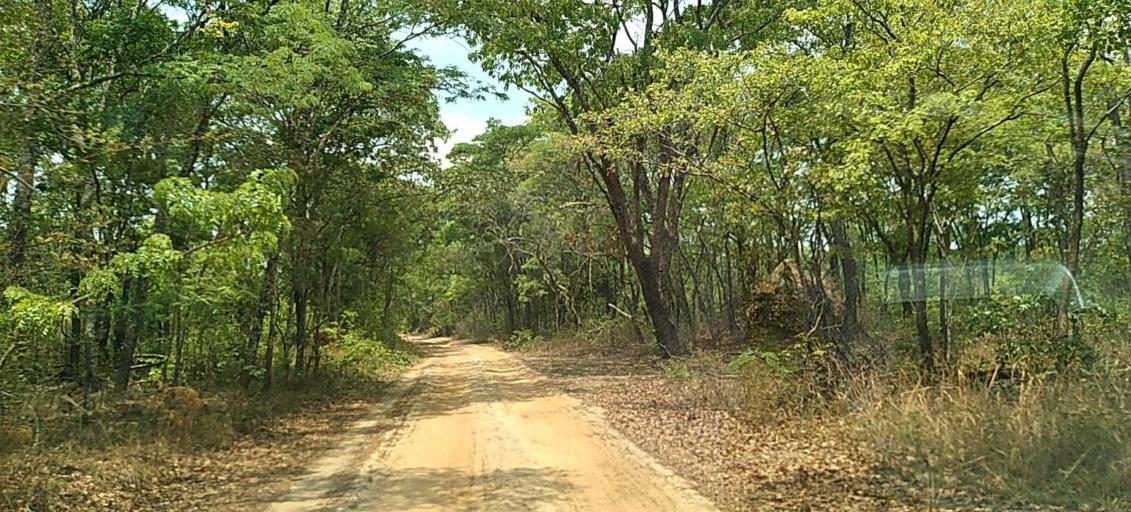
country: ZM
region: Copperbelt
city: Chingola
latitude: -12.7709
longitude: 27.6893
